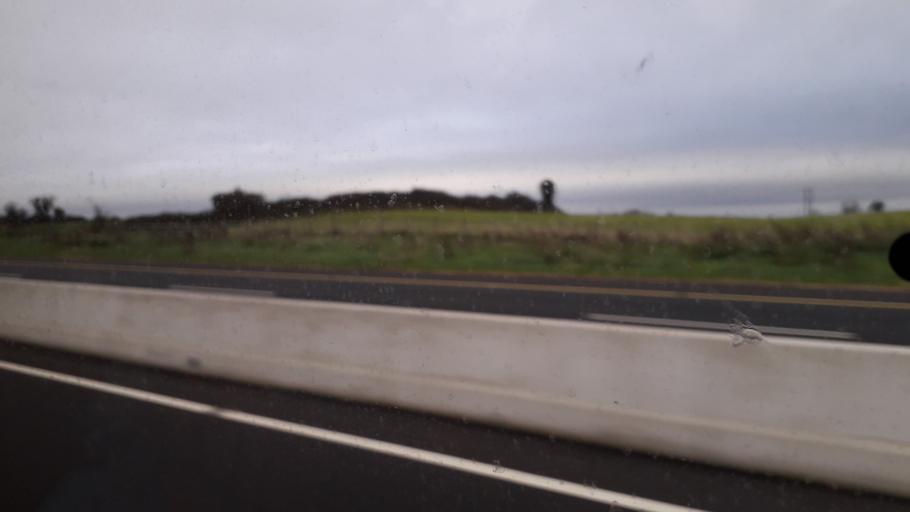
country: IE
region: Connaught
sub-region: County Galway
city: Athenry
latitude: 53.2730
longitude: -8.8044
